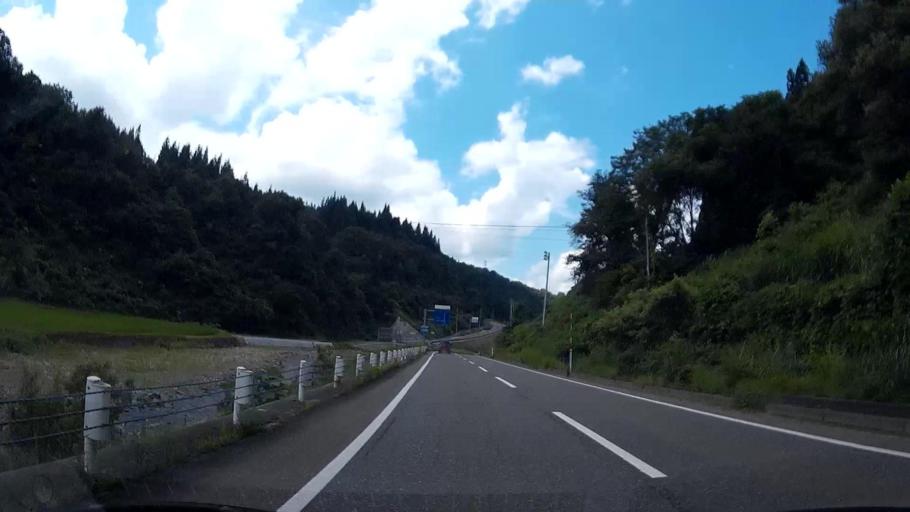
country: JP
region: Niigata
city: Shiozawa
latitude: 37.0479
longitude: 138.7683
